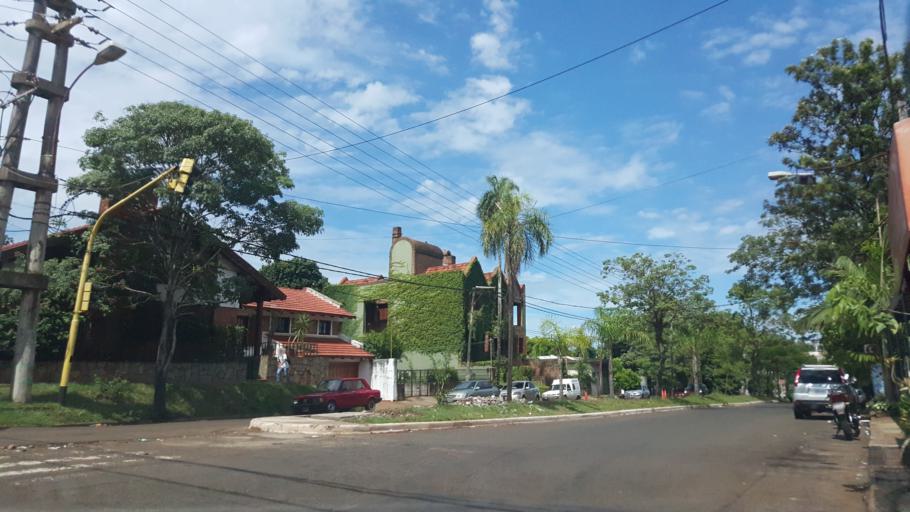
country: AR
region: Misiones
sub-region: Departamento de Capital
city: Posadas
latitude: -27.3604
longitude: -55.9005
